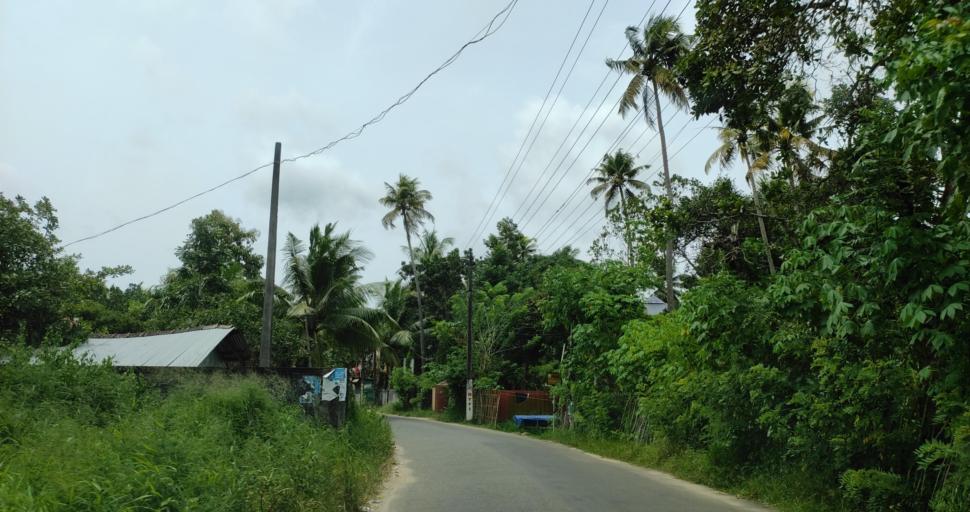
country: IN
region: Kerala
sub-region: Alappuzha
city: Shertallai
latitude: 9.6744
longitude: 76.3550
